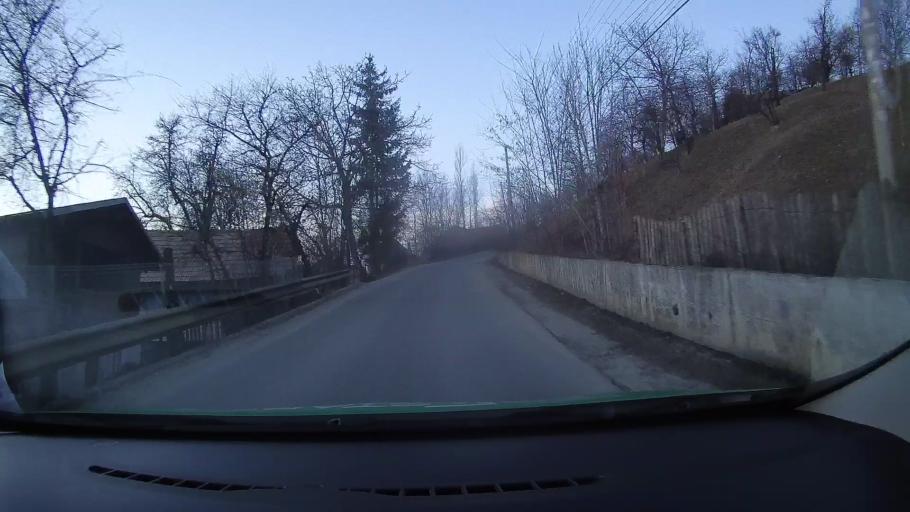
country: RO
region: Prahova
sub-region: Comuna Comarnic
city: Comarnic
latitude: 45.2470
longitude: 25.6422
